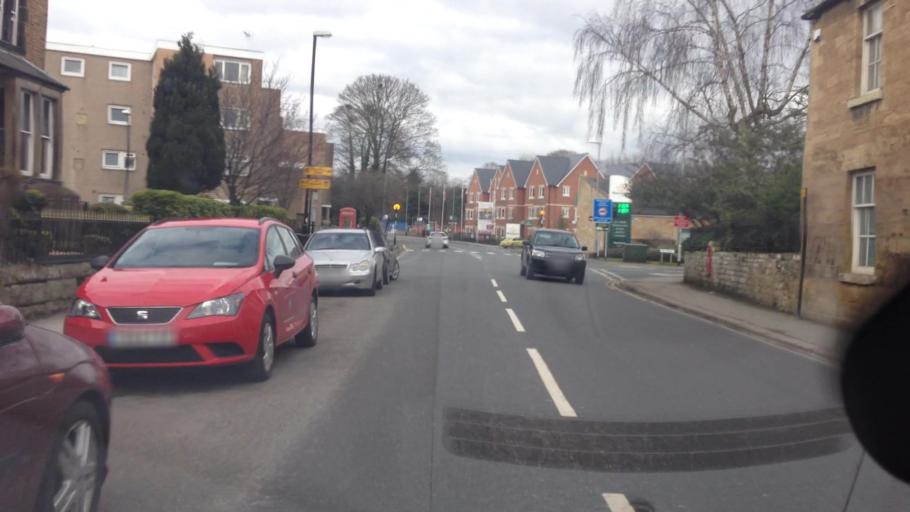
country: GB
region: England
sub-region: City and Borough of Leeds
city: Wetherby
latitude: 53.9313
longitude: -1.3842
